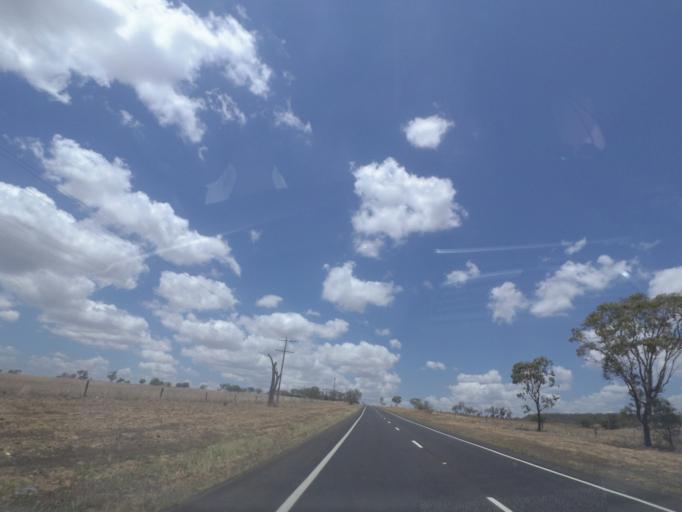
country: AU
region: Queensland
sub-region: Toowoomba
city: Top Camp
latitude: -27.7255
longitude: 151.9117
